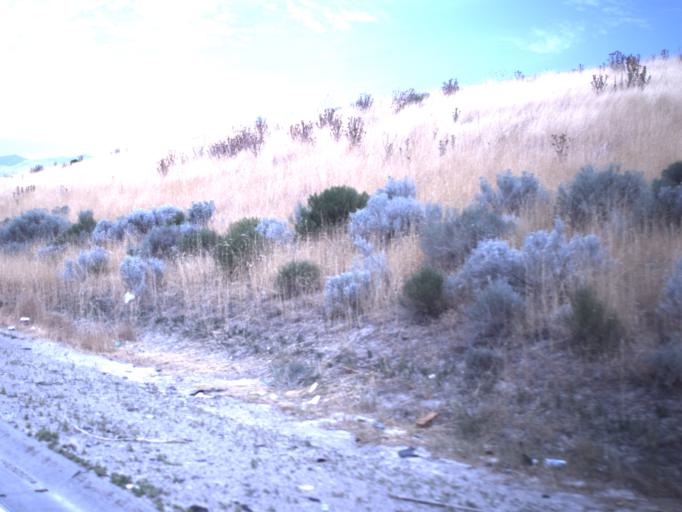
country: US
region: Utah
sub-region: Salt Lake County
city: Bluffdale
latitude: 40.4970
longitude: -111.9147
